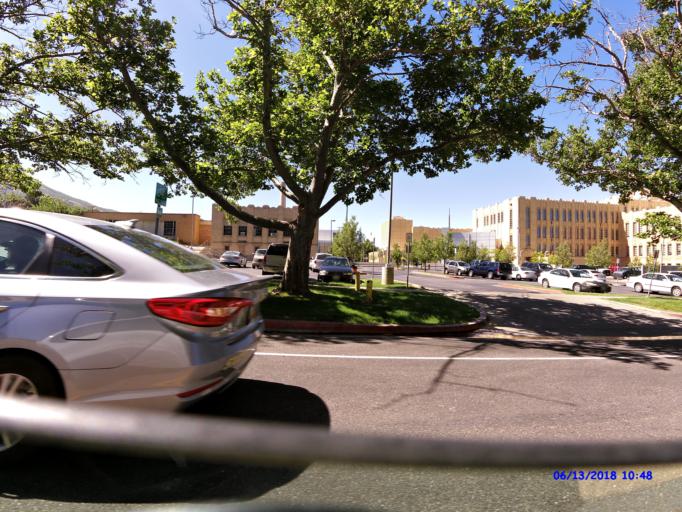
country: US
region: Utah
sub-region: Weber County
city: Ogden
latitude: 41.2141
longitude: -111.9464
